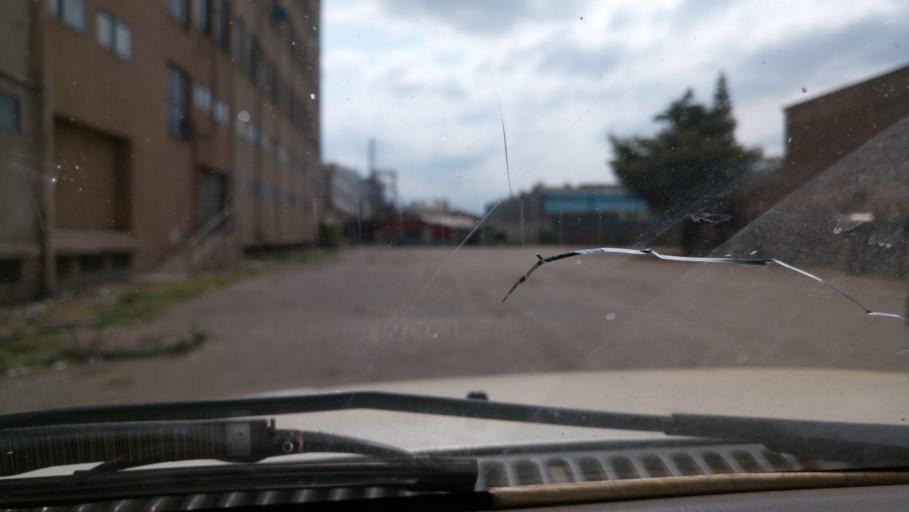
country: KE
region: Nairobi Area
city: Pumwani
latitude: -1.3281
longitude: 36.8555
